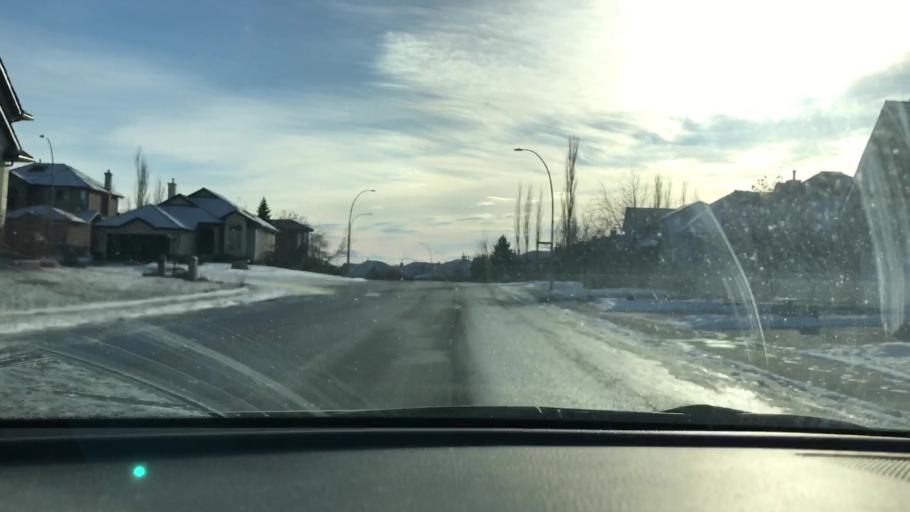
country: CA
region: Alberta
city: Calgary
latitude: 51.0243
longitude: -114.1772
